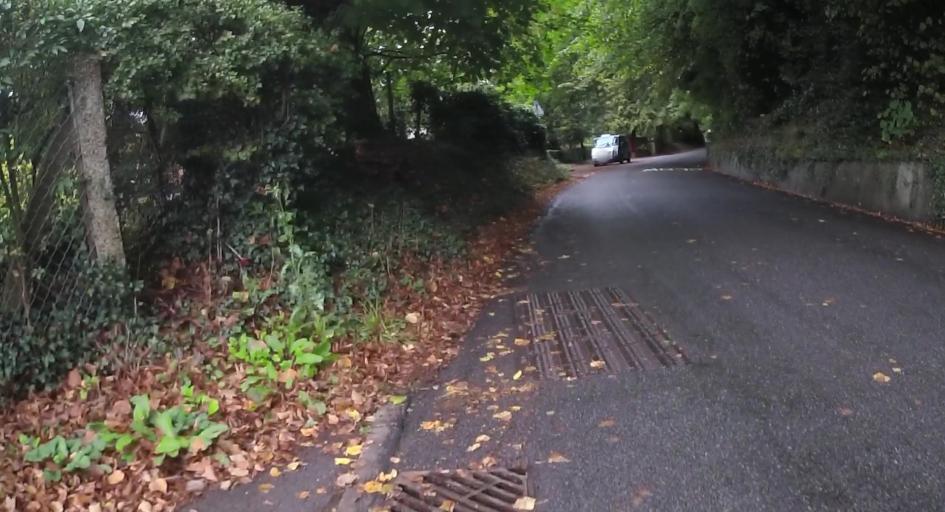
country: GB
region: England
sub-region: Hampshire
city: Tadley
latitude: 51.3989
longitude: -1.1778
